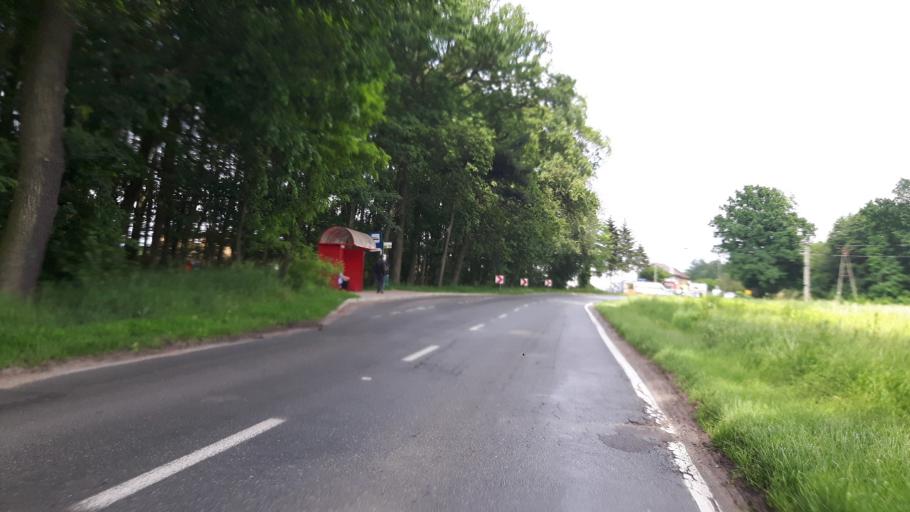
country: PL
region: West Pomeranian Voivodeship
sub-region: Powiat gryfinski
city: Stare Czarnowo
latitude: 53.4268
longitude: 14.7169
